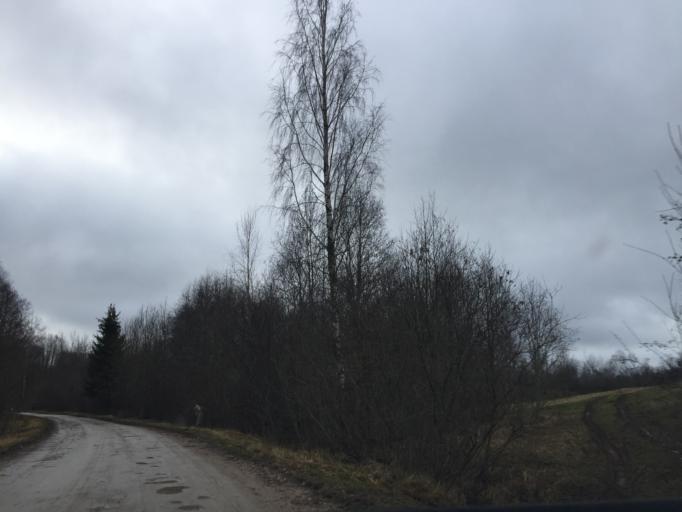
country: LV
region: Broceni
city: Broceni
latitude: 56.6643
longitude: 22.5520
